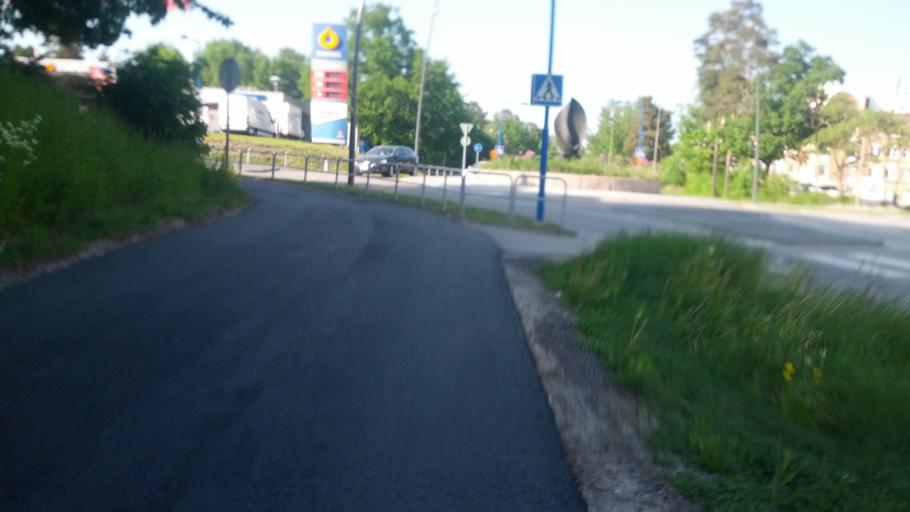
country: SE
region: Stockholm
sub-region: Danderyds Kommun
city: Djursholm
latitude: 59.3950
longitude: 18.0508
